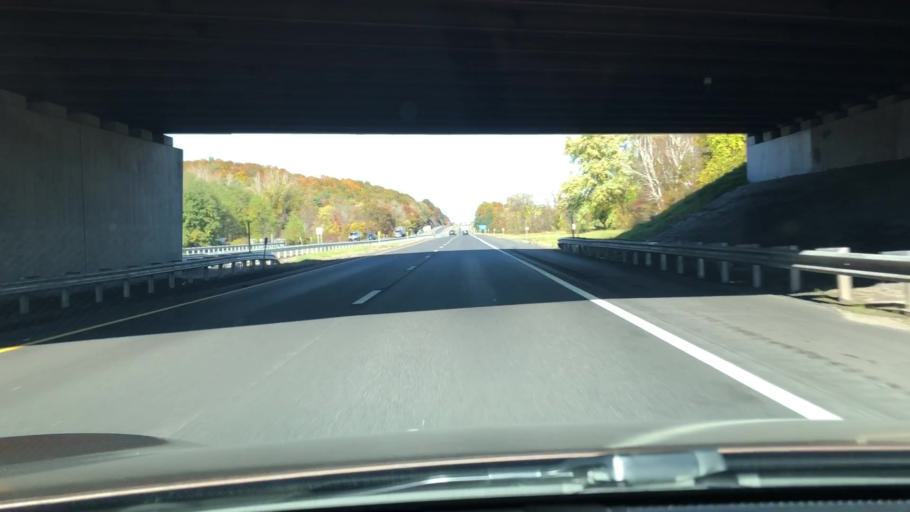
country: US
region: New York
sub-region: Ulster County
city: Lake Katrine
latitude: 41.9760
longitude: -74.0112
